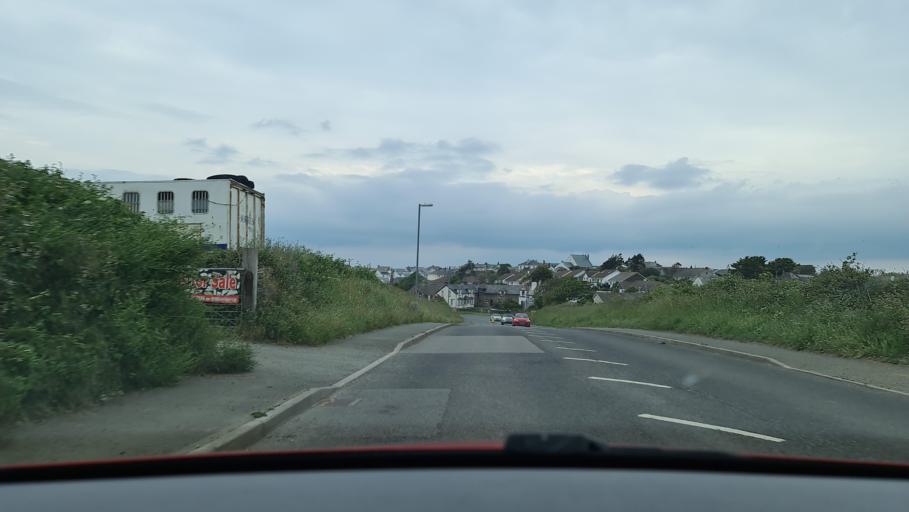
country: GB
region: England
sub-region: Cornwall
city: Tintagel
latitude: 50.6588
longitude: -4.7490
